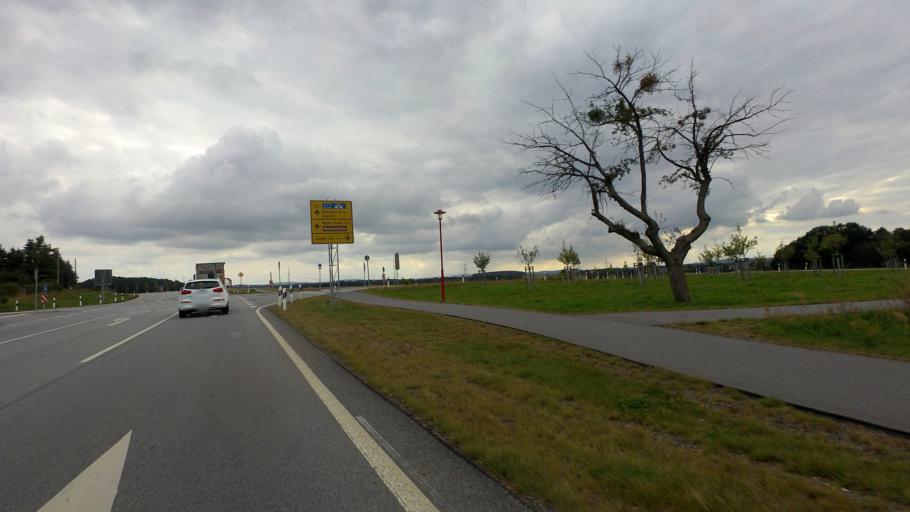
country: DE
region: Saxony
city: Neschwitz
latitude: 51.2490
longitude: 14.3557
